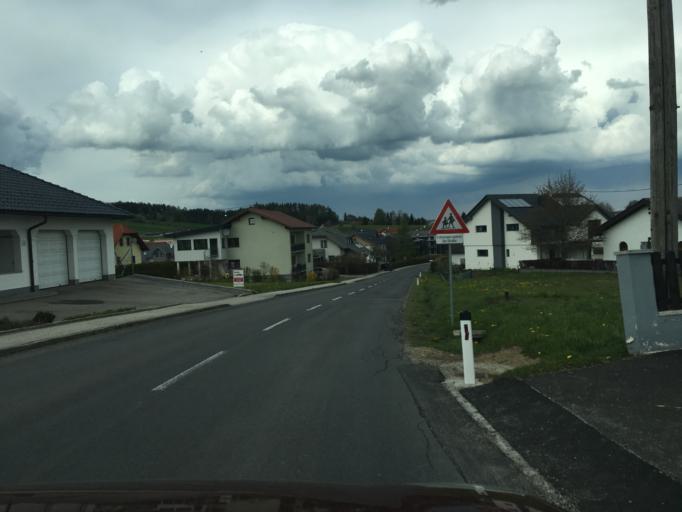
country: AT
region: Upper Austria
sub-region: Politischer Bezirk Urfahr-Umgebung
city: Reichenthal
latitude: 48.5399
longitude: 14.3724
